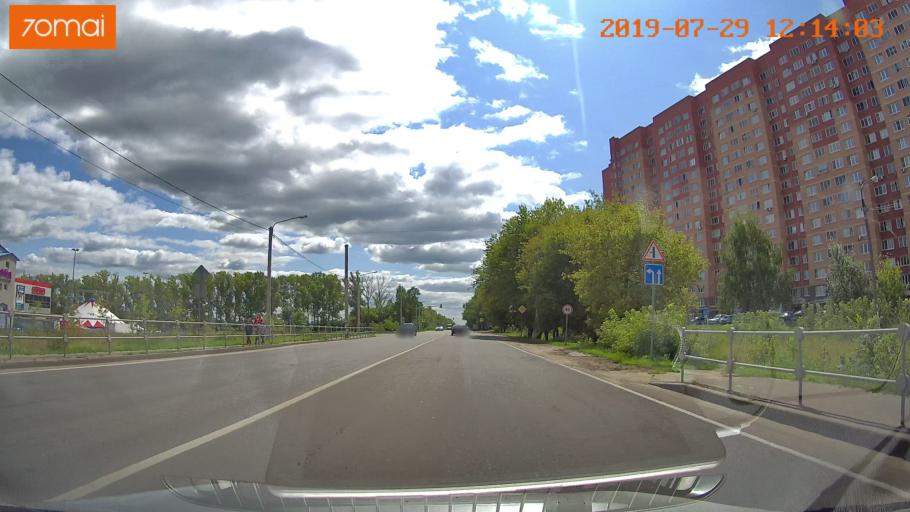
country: RU
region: Moskovskaya
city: Voskresensk
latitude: 55.3129
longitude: 38.6538
